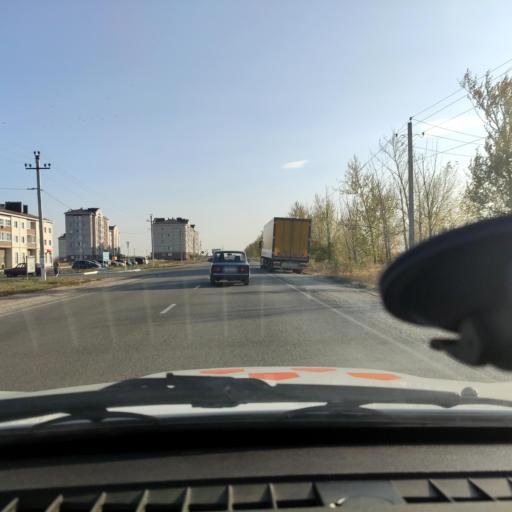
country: RU
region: Voronezj
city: Novaya Usman'
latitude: 51.6044
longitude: 39.3735
